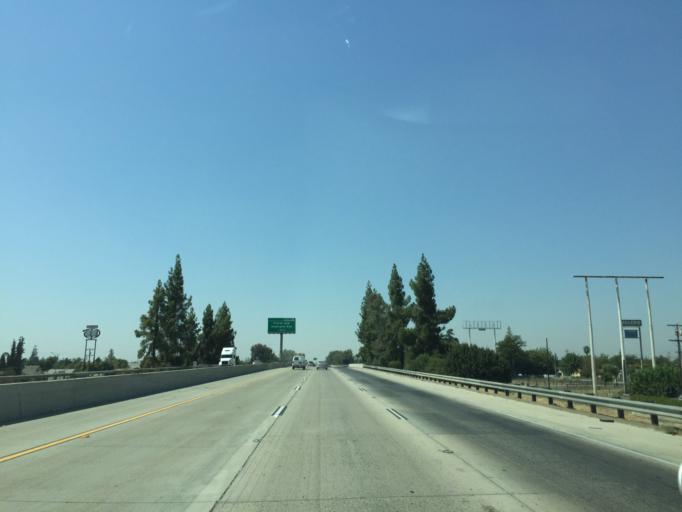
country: US
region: California
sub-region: Fresno County
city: Selma
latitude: 36.5628
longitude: -119.6144
